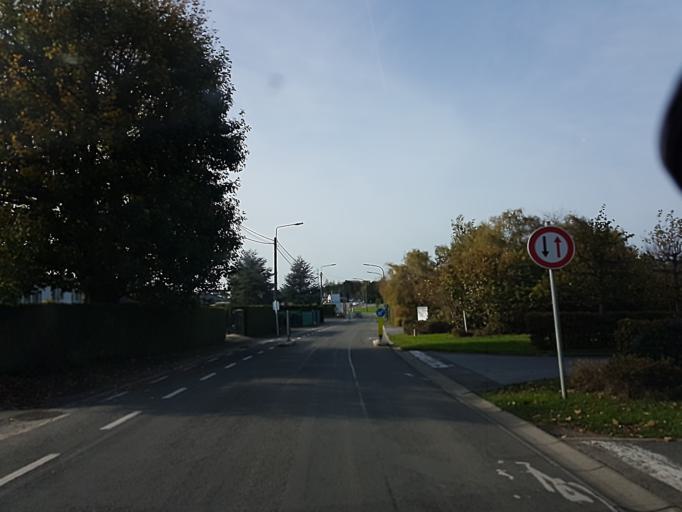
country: BE
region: Wallonia
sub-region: Province de Liege
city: Seraing
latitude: 50.5399
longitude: 5.4658
